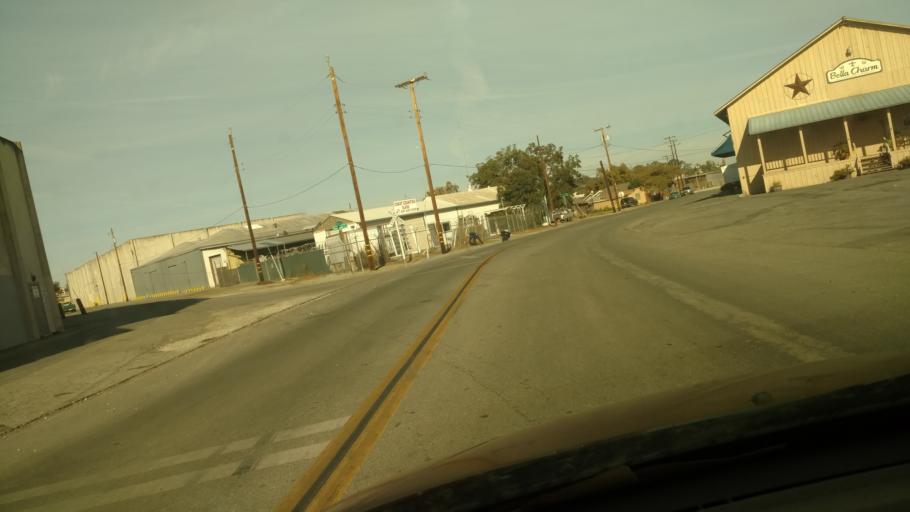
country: US
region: California
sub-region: San Benito County
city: Hollister
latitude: 36.8468
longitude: -121.3964
